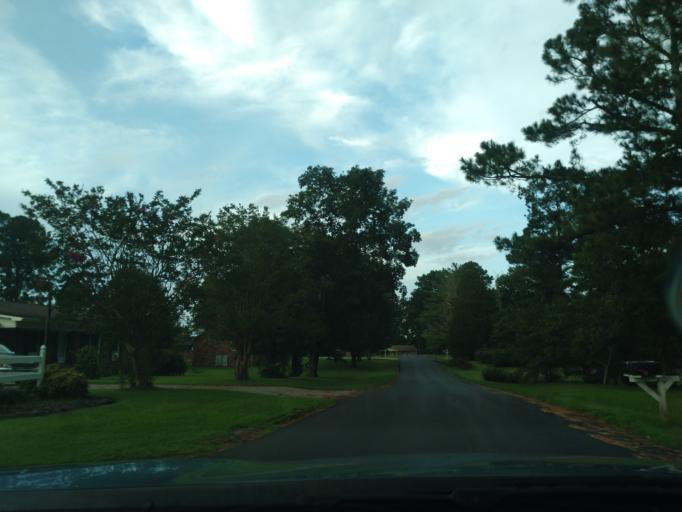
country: US
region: North Carolina
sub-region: Washington County
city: Plymouth
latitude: 35.8295
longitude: -76.7768
